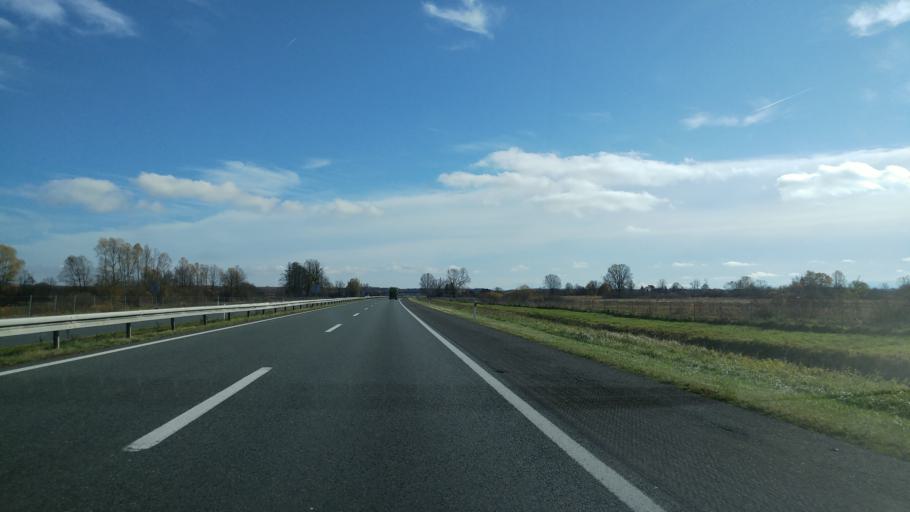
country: HR
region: Sisacko-Moslavacka
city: Lipovljani
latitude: 45.3637
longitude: 16.8964
